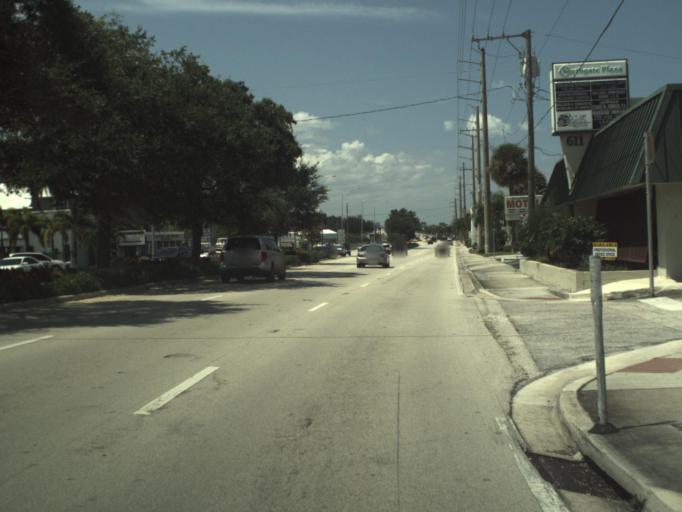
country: US
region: Florida
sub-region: Martin County
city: Stuart
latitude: 27.1944
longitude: -80.2569
